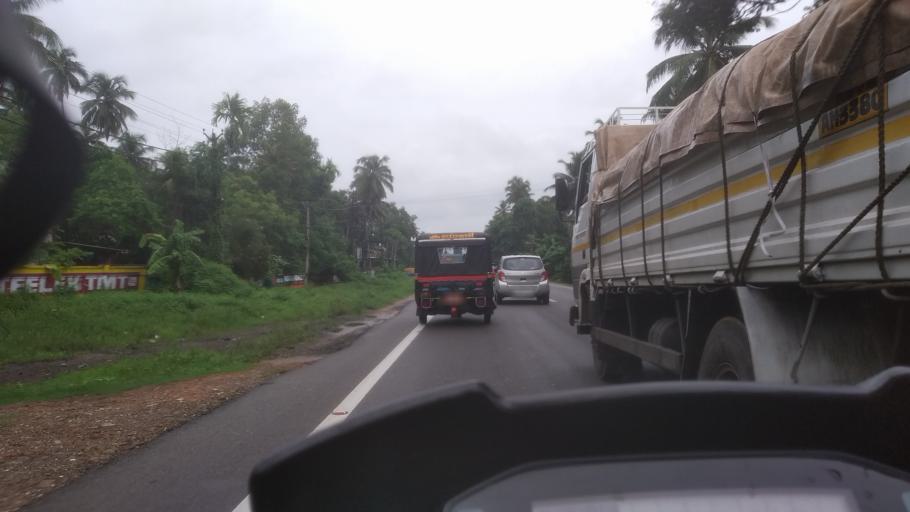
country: IN
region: Kerala
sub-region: Alappuzha
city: Kayankulam
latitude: 9.1675
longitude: 76.5006
